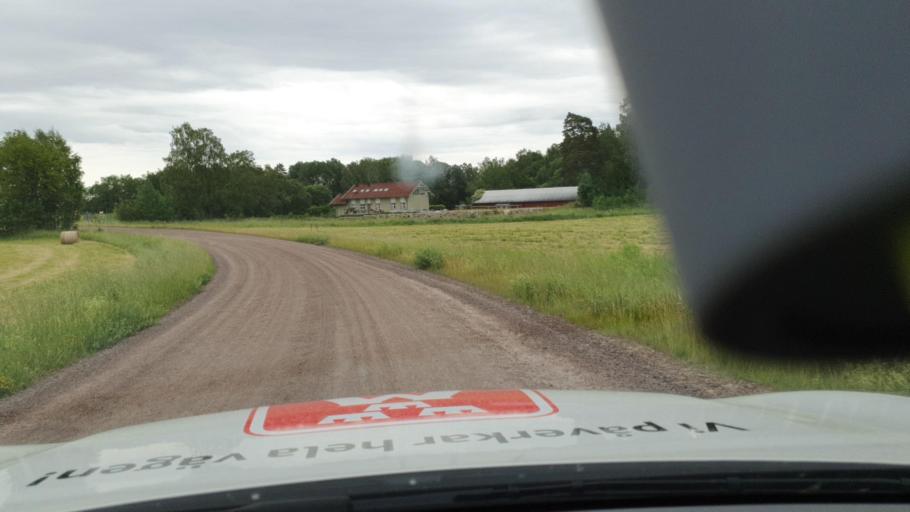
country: SE
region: Vaestra Goetaland
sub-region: Skovde Kommun
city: Skoevde
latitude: 58.3698
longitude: 13.8703
